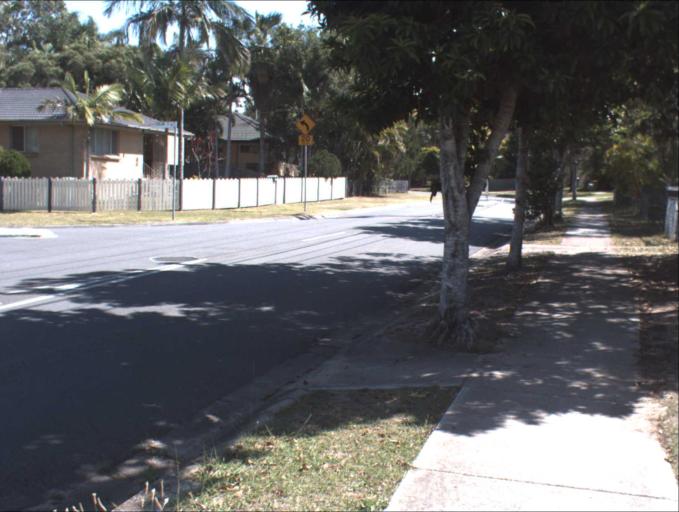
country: AU
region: Queensland
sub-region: Logan
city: Rochedale South
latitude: -27.5918
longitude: 153.1324
